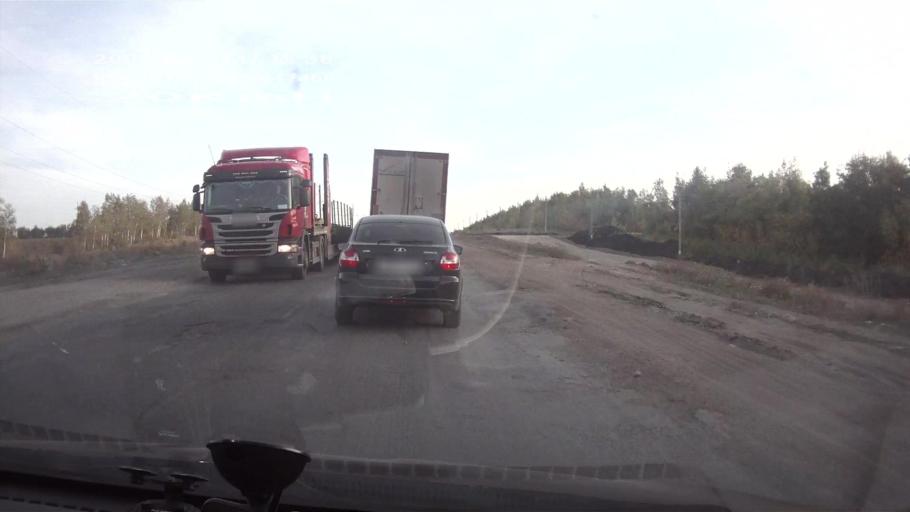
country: RU
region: Saratov
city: Krasnoarmeysk
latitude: 51.2070
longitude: 45.6475
